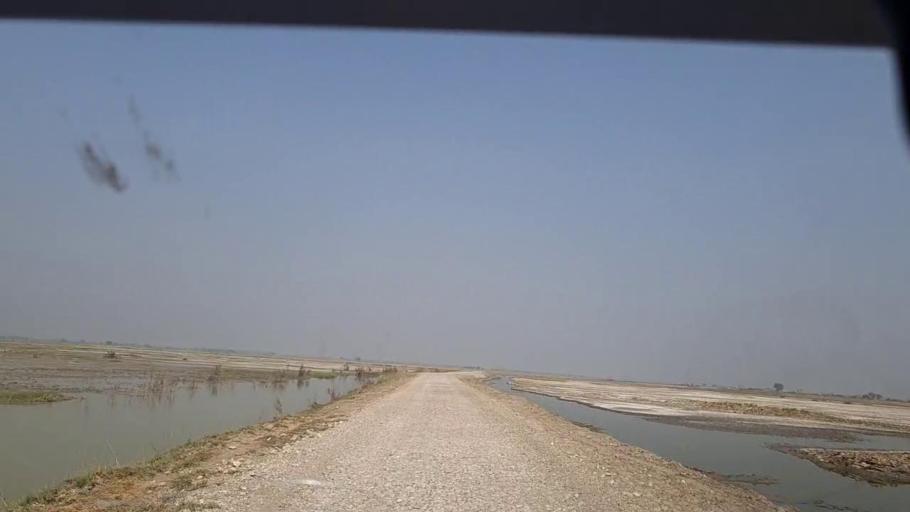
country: PK
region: Sindh
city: Shikarpur
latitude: 28.0442
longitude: 68.6520
